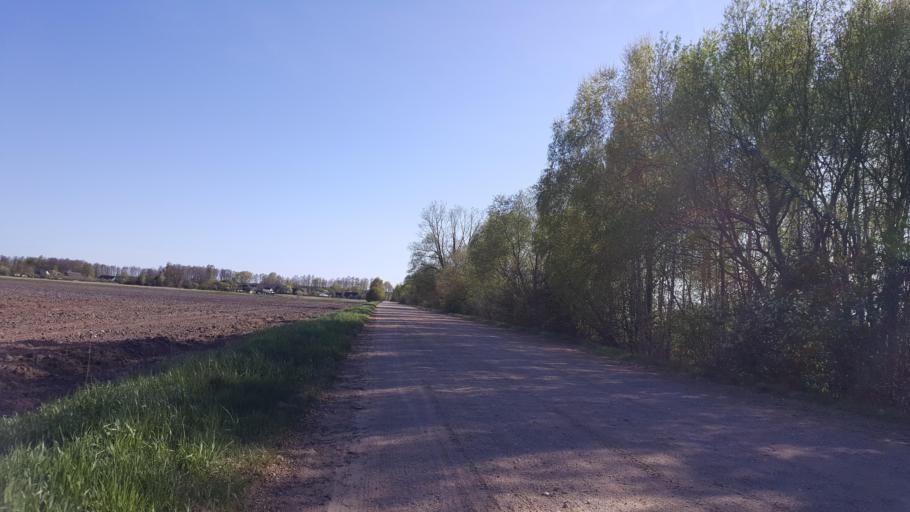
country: BY
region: Brest
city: Kamyanyets
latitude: 52.4272
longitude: 23.8810
